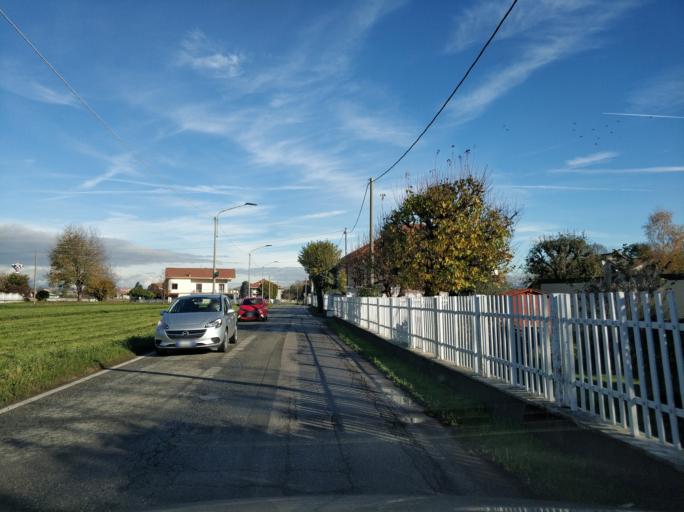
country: IT
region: Piedmont
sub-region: Provincia di Torino
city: Cirie
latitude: 45.2265
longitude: 7.5842
